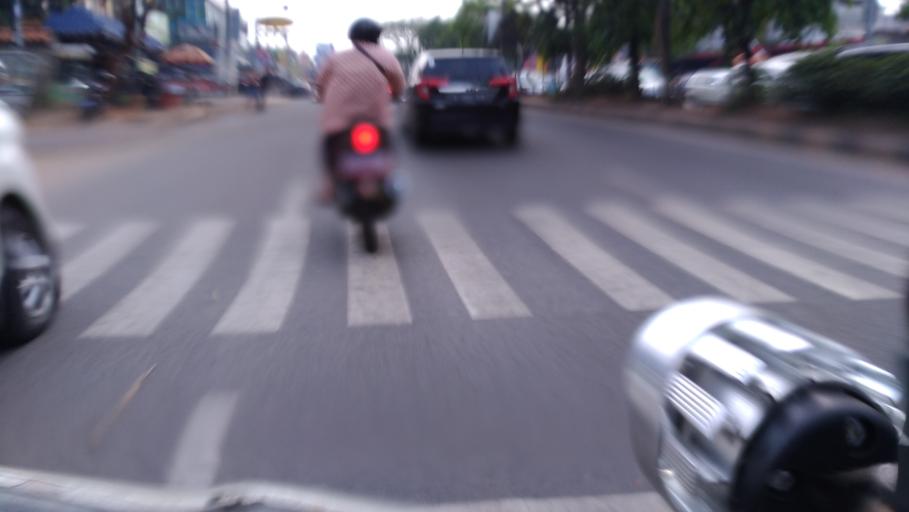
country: ID
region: West Java
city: Cileungsir
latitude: -6.3760
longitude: 106.9006
